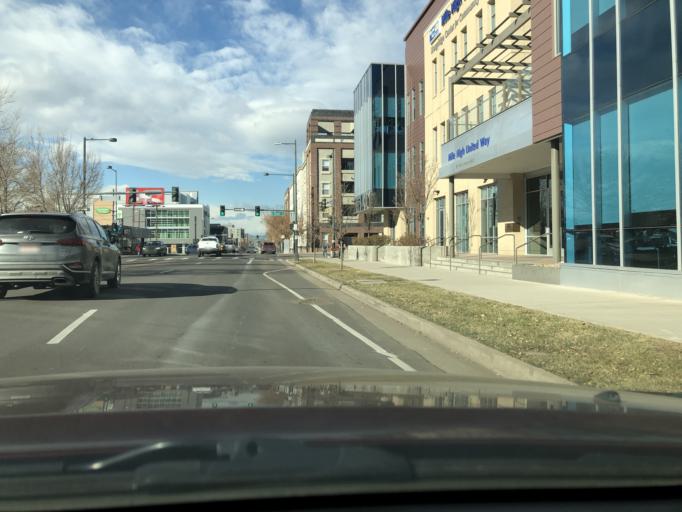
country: US
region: Colorado
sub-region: Denver County
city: Denver
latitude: 39.7520
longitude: -104.9840
